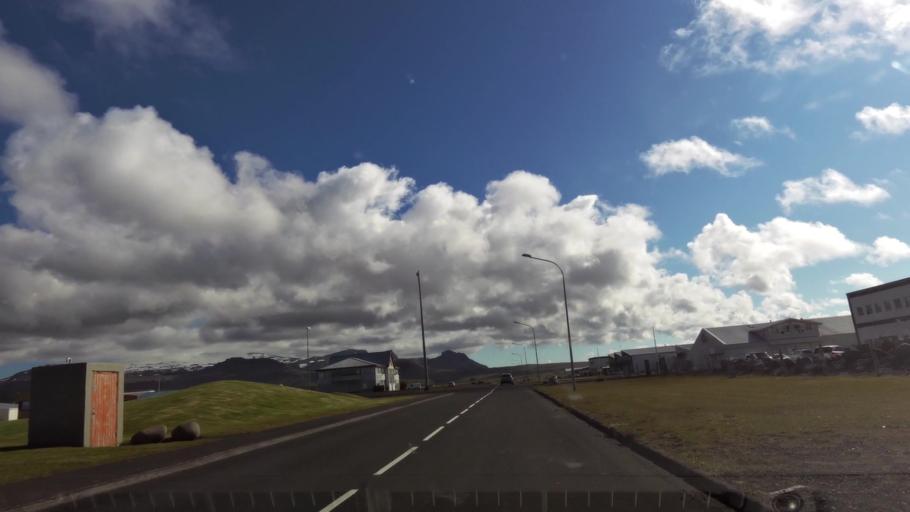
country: IS
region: West
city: Olafsvik
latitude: 64.9238
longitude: -23.8156
